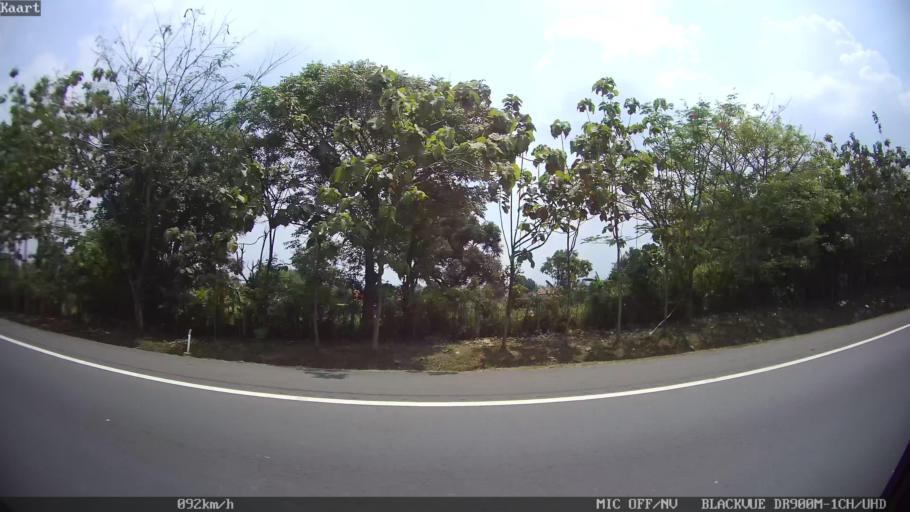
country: ID
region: Banten
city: Serang
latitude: -6.0829
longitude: 106.1346
